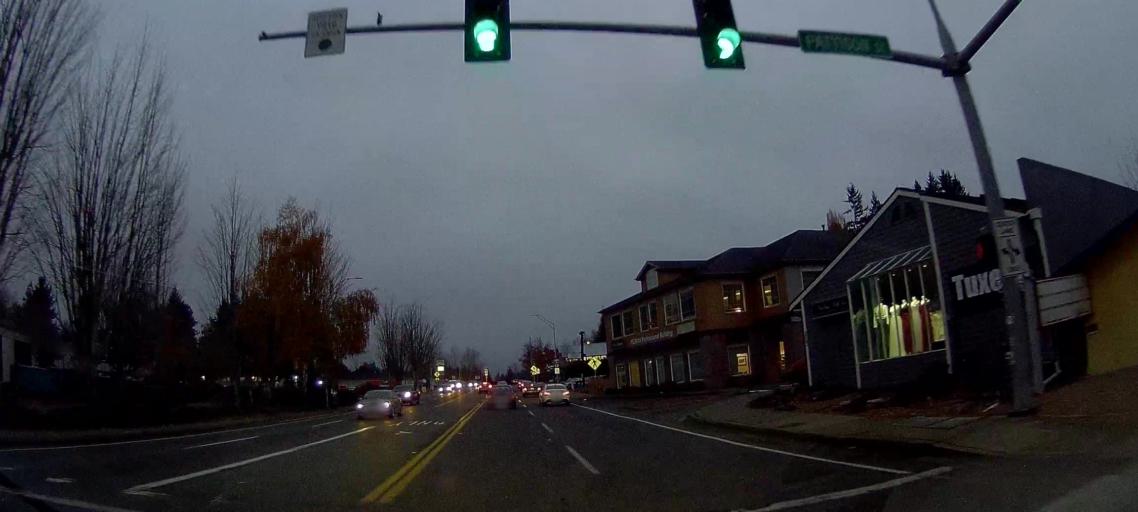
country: US
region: Washington
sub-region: Thurston County
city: Lacey
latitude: 47.0430
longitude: -122.8590
